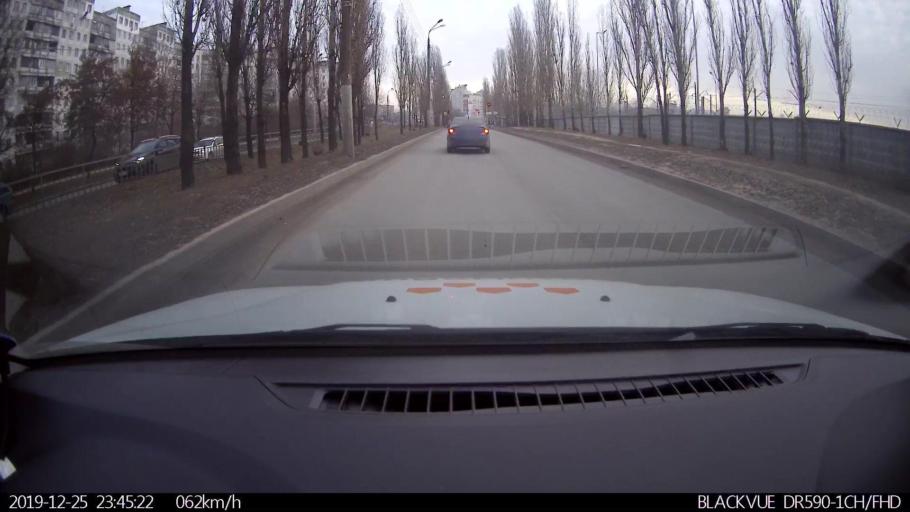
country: RU
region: Nizjnij Novgorod
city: Nizhniy Novgorod
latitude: 56.3310
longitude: 43.9416
